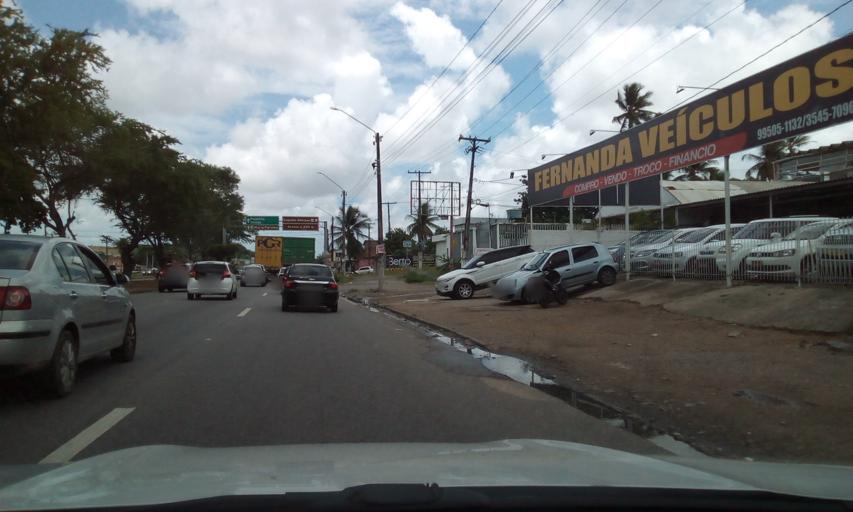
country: BR
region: Pernambuco
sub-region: Igarassu
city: Igarassu
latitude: -7.8623
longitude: -34.9079
